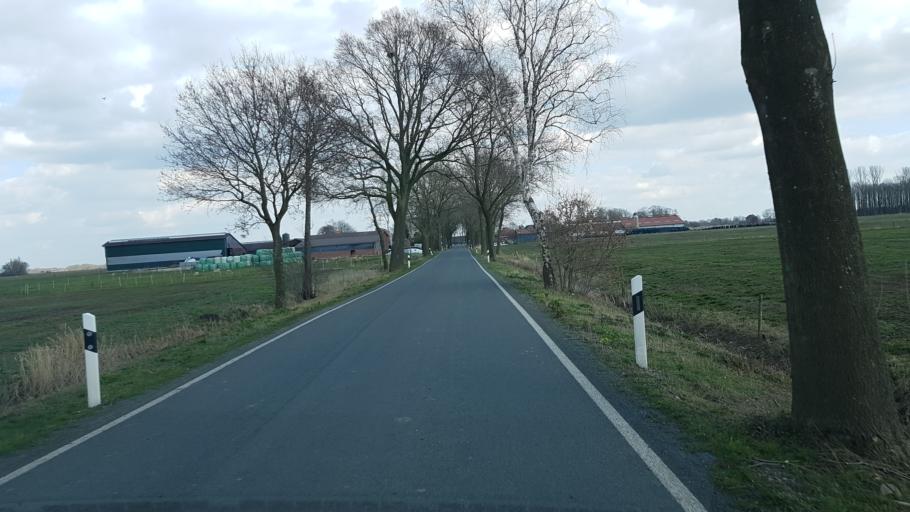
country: DE
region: Lower Saxony
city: Rastede
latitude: 53.3101
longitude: 8.2425
